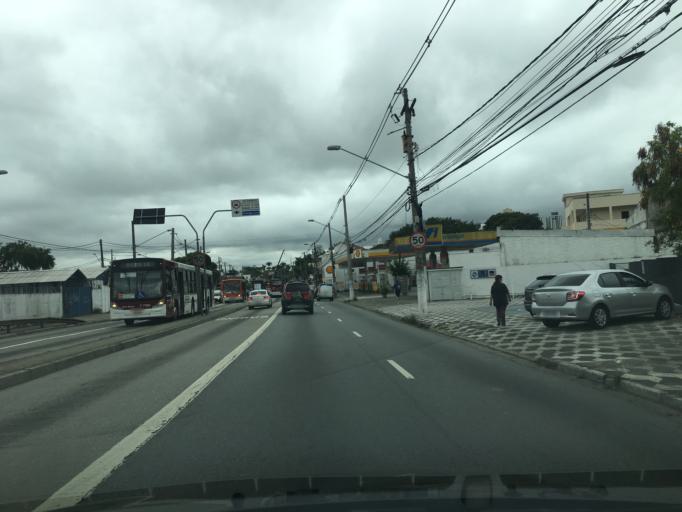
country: BR
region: Sao Paulo
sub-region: Taboao Da Serra
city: Taboao da Serra
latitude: -23.5889
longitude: -46.7286
